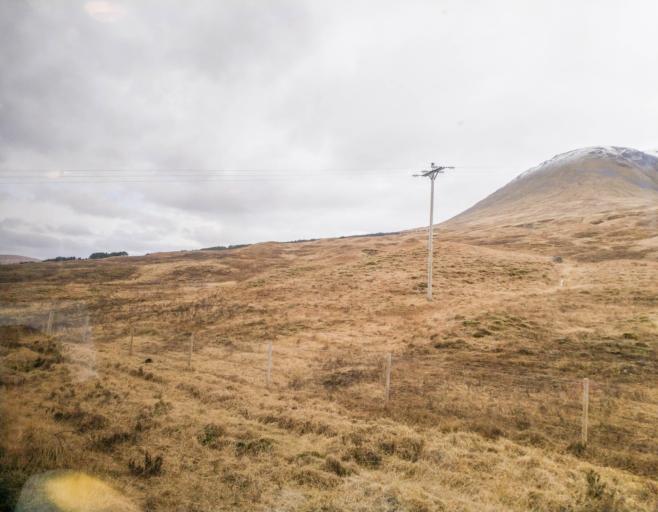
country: GB
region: Scotland
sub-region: Highland
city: Spean Bridge
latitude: 56.5127
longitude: -4.7615
